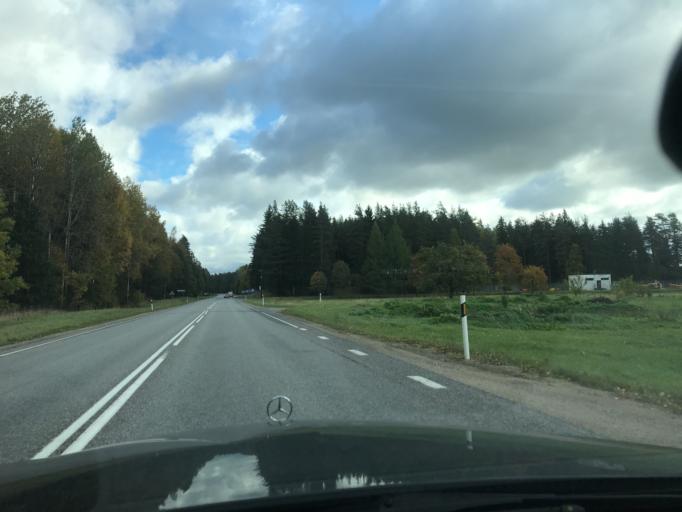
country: EE
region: Vorumaa
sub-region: Voru linn
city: Voru
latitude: 57.7390
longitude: 27.2708
